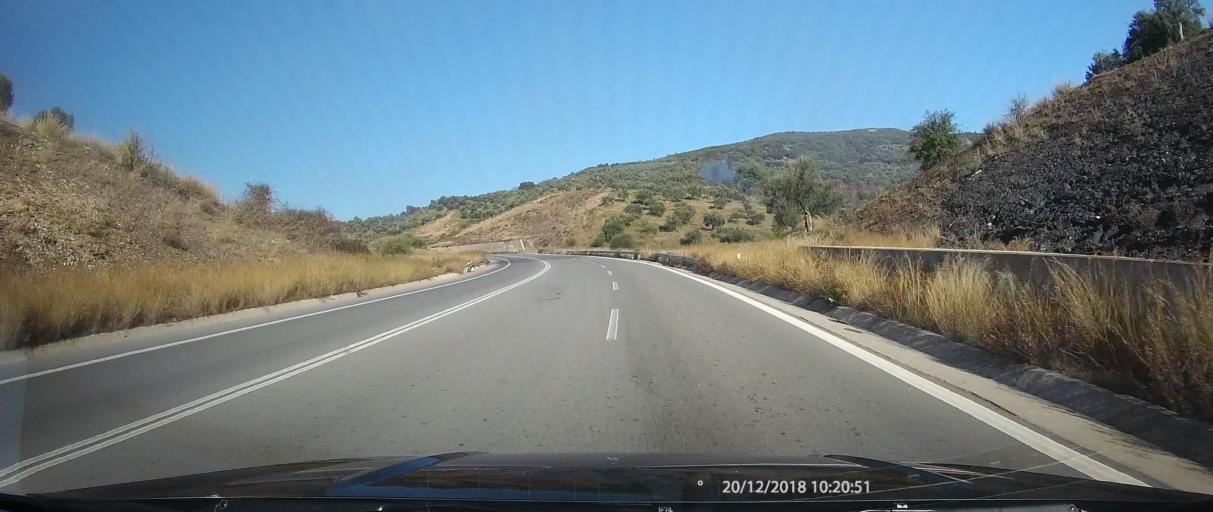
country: GR
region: Peloponnese
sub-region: Nomos Lakonias
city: Magoula
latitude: 37.1535
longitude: 22.4333
